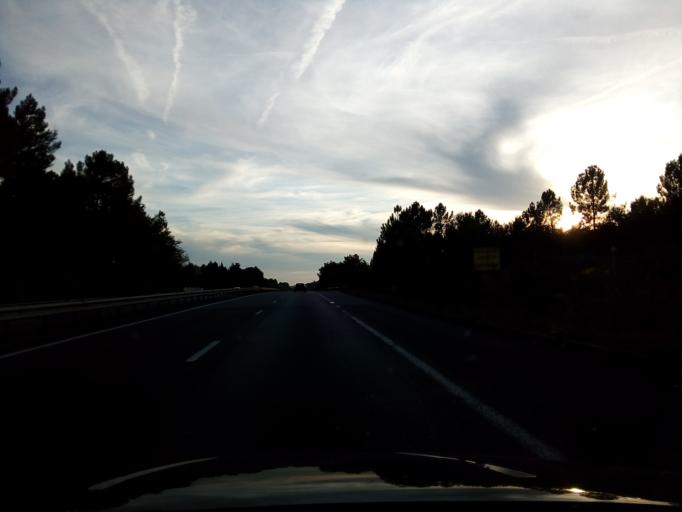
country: FR
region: Aquitaine
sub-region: Departement de la Gironde
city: Laruscade
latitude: 45.1923
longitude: -0.3123
